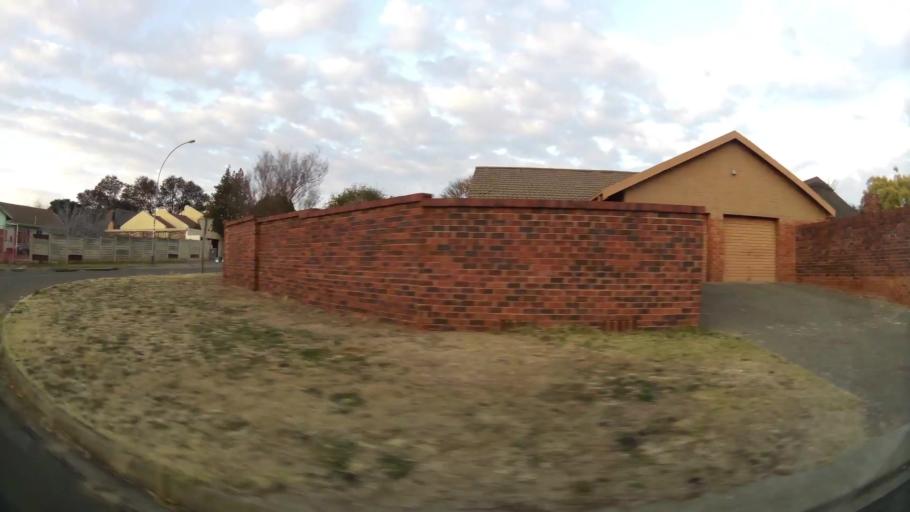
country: ZA
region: Orange Free State
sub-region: Mangaung Metropolitan Municipality
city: Bloemfontein
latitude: -29.1631
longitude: 26.1849
